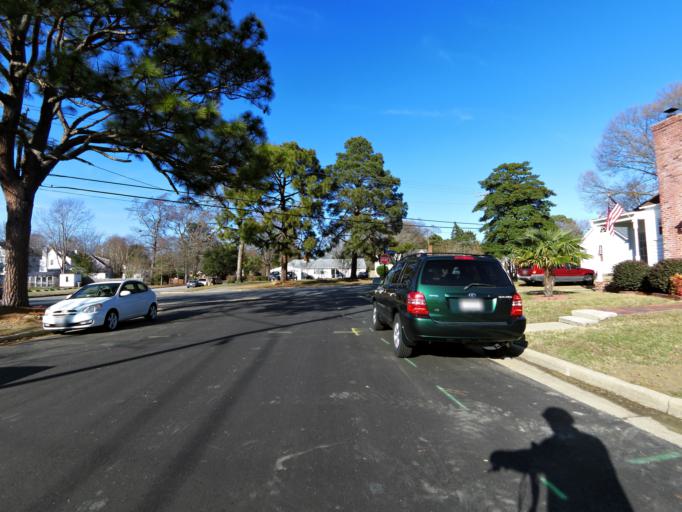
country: US
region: Virginia
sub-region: City of Hampton
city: Hampton
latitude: 37.0063
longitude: -76.3712
